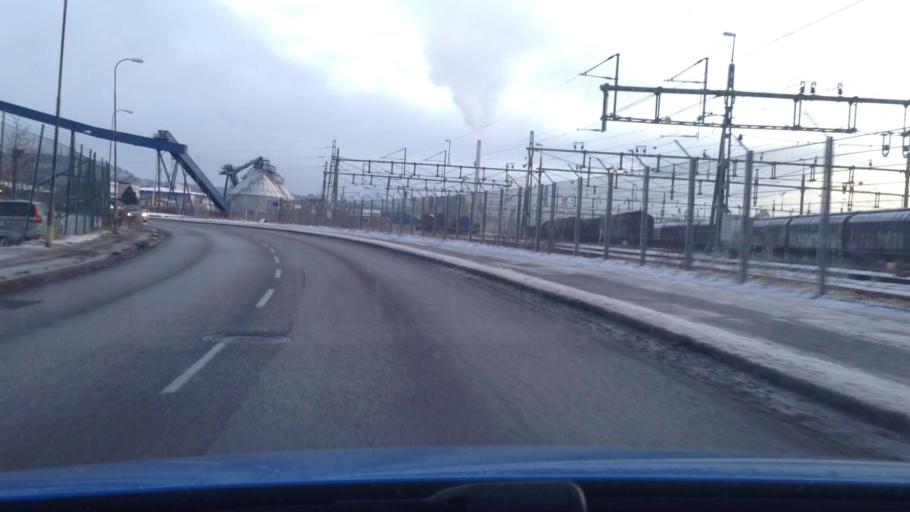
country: SE
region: Vaestra Goetaland
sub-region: Goteborg
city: Eriksbo
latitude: 57.7278
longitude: 12.0321
